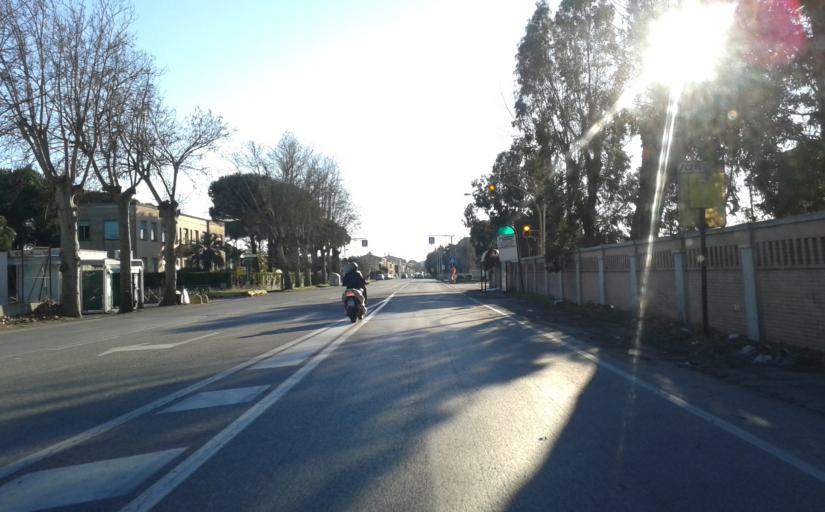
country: IT
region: Tuscany
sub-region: Provincia di Livorno
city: Livorno
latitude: 43.5839
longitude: 10.3446
